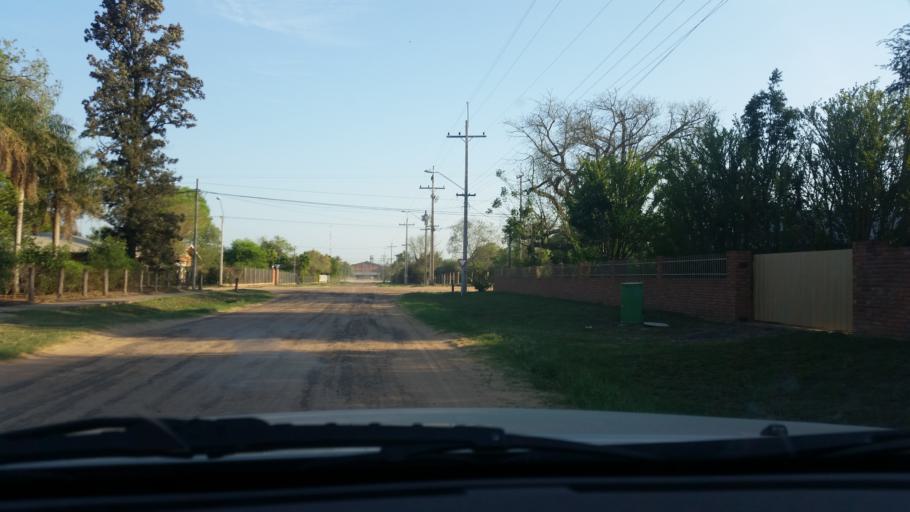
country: PY
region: Boqueron
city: Filadelfia
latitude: -22.3478
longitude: -60.0388
